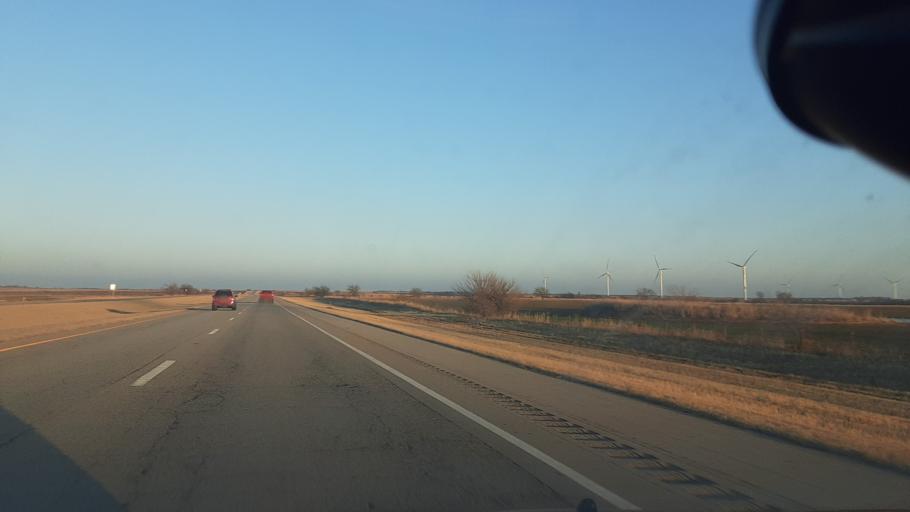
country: US
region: Oklahoma
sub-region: Noble County
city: Perry
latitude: 36.3979
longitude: -97.4034
